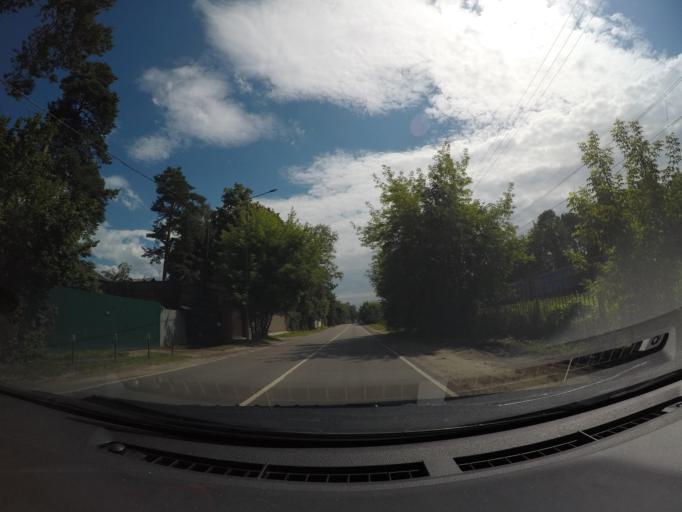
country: RU
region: Moskovskaya
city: Malakhovka
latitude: 55.6435
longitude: 38.0165
